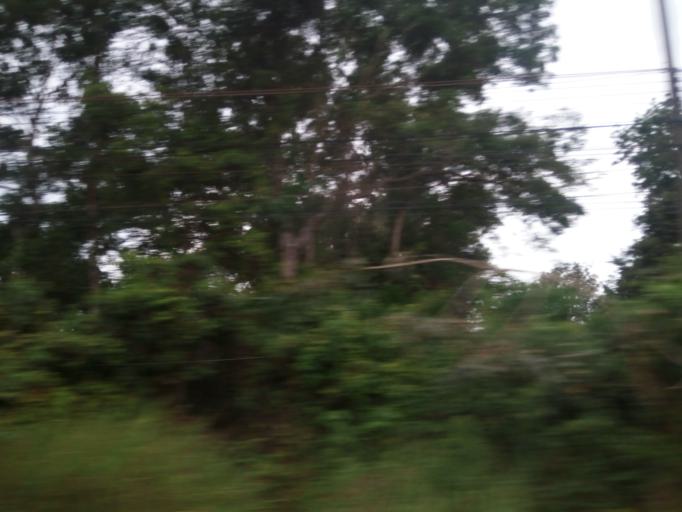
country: TH
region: Phuket
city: Thalang
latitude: 8.0558
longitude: 98.4067
